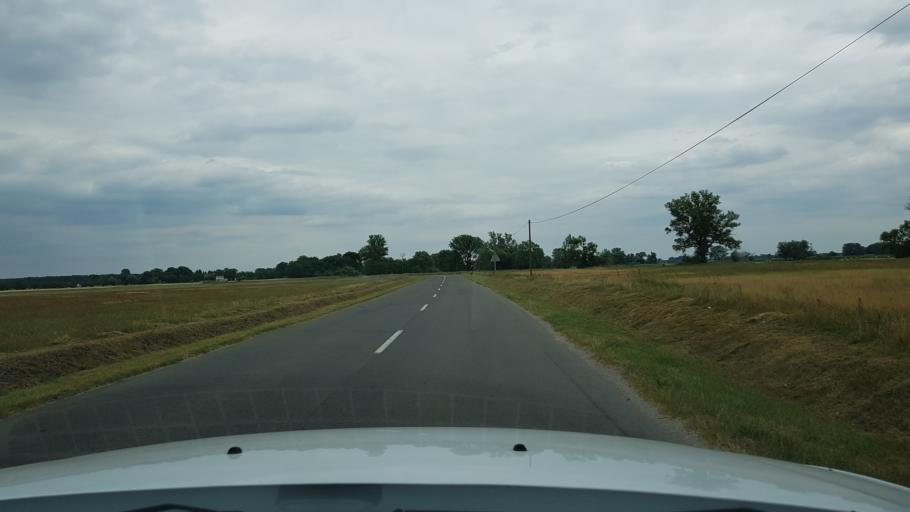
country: DE
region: Brandenburg
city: Manschnow
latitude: 52.6287
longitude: 14.5688
